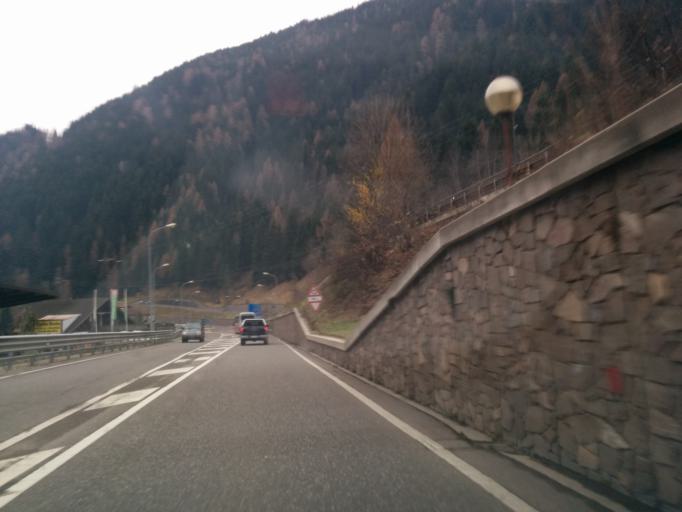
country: IT
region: Trentino-Alto Adige
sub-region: Provincia di Trento
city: Predazzo
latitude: 46.3208
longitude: 11.5969
